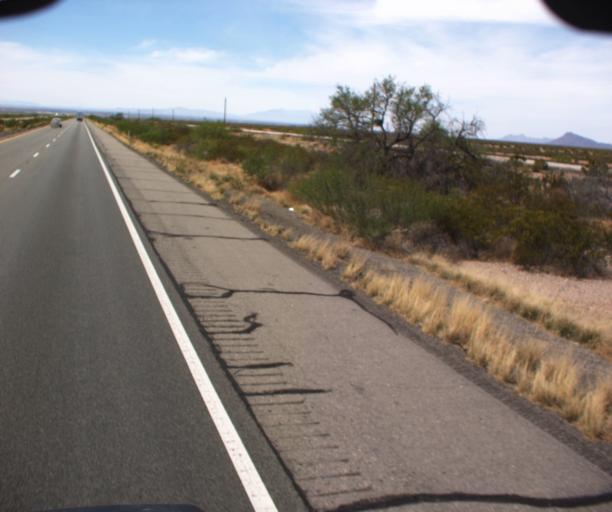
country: US
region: New Mexico
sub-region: Hidalgo County
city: Lordsburg
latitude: 32.2454
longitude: -109.1257
